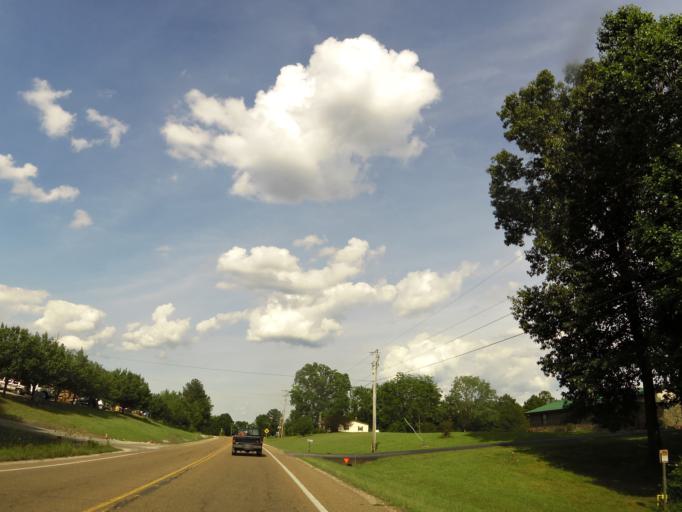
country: US
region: Tennessee
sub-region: Carroll County
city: Bruceton
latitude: 36.0353
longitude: -88.1956
